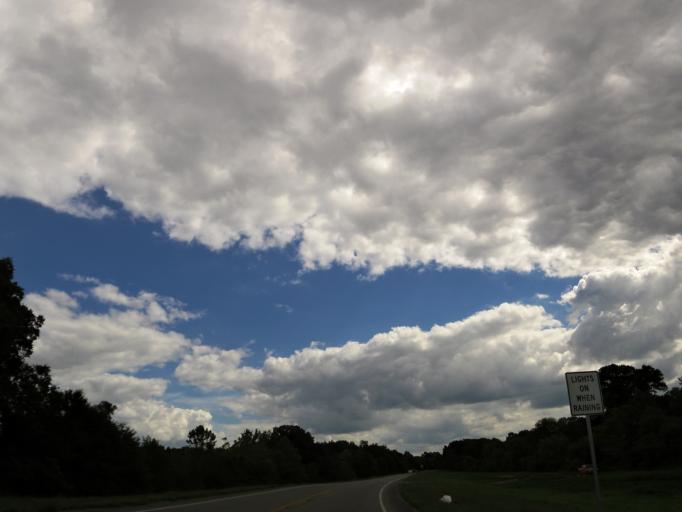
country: US
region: Tennessee
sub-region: Hamilton County
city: Lookout Mountain
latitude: 34.9769
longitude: -85.3329
